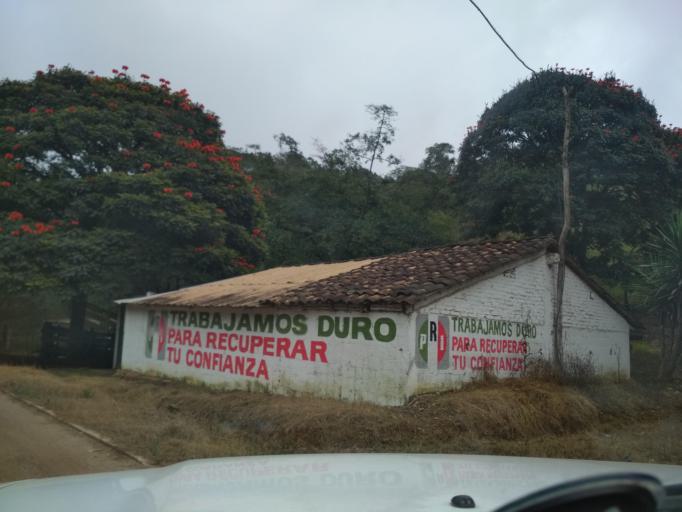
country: MX
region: Veracruz
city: El Castillo
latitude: 19.5440
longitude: -96.8332
